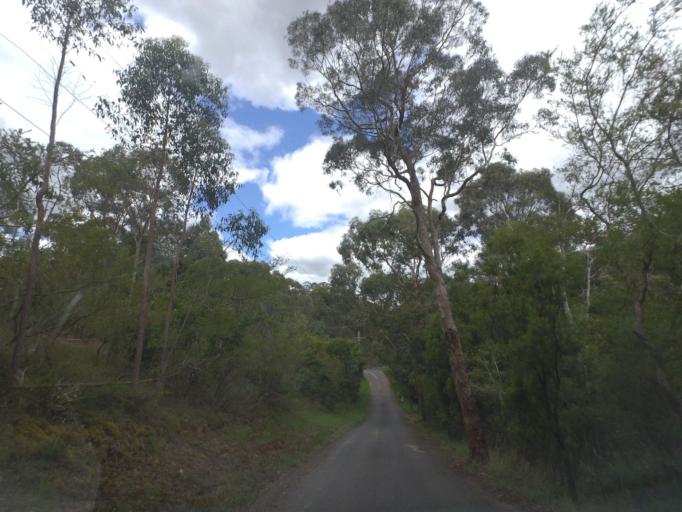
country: AU
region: Victoria
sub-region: Manningham
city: Park Orchards
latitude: -37.7762
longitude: 145.1968
